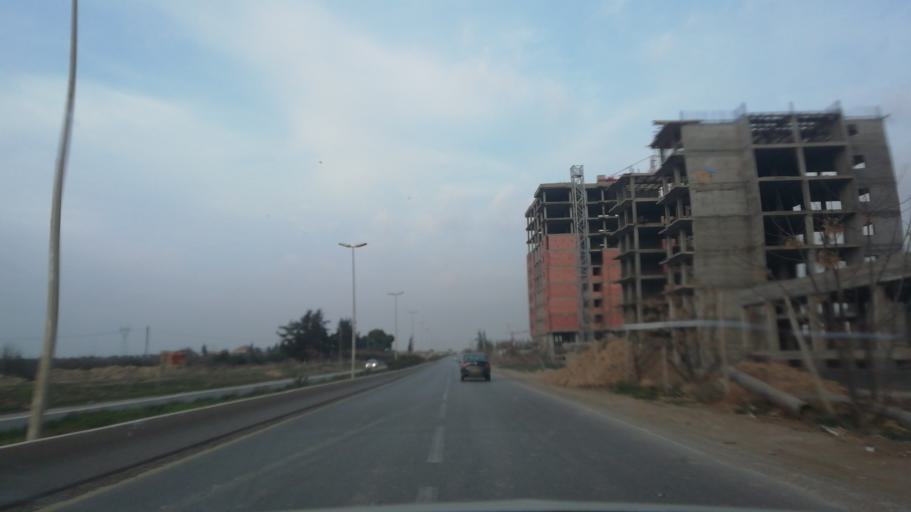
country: DZ
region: Sidi Bel Abbes
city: Sidi Bel Abbes
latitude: 35.2136
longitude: -0.6539
